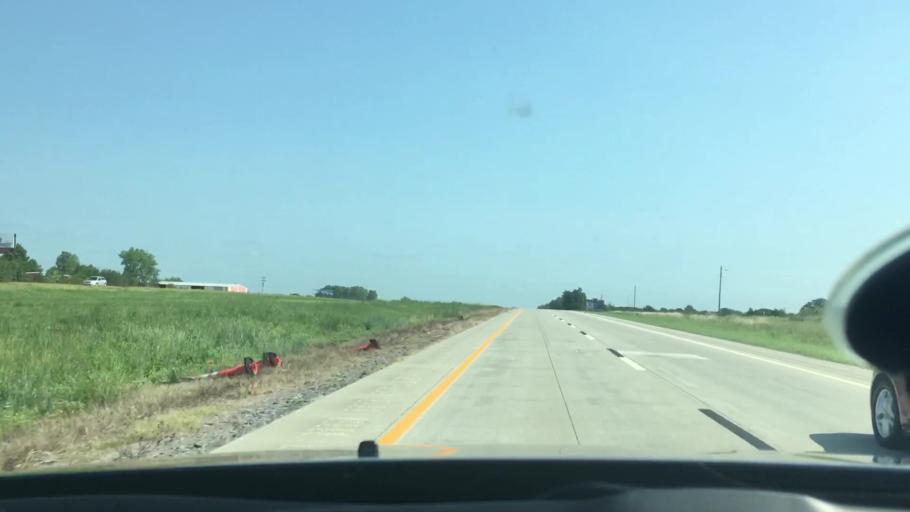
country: US
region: Oklahoma
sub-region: Atoka County
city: Atoka
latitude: 34.1939
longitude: -96.2412
